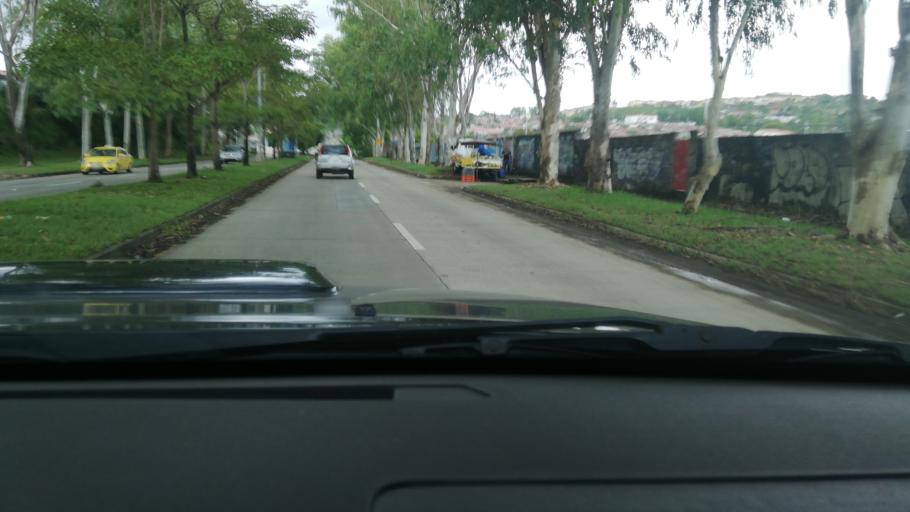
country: PA
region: Panama
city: San Miguelito
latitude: 9.0443
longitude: -79.4819
